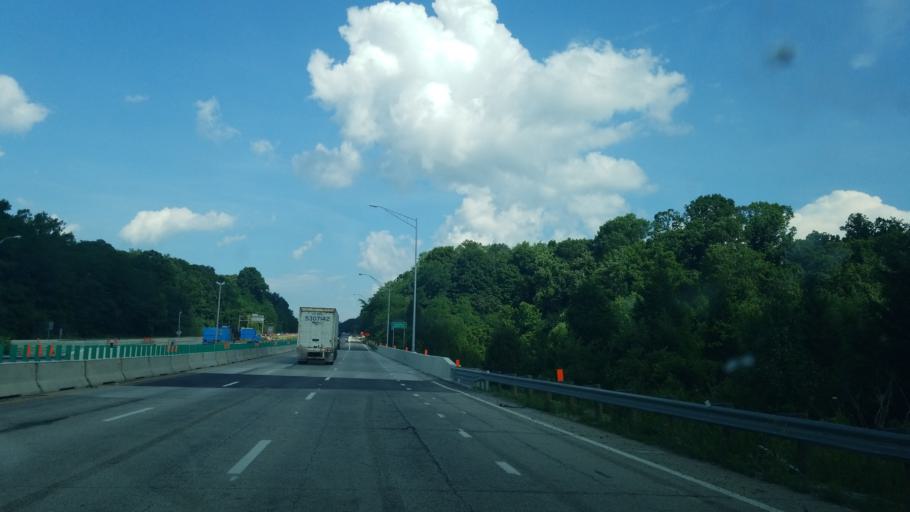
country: US
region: Kentucky
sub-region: Campbell County
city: Silver Grove
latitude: 39.0588
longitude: -84.4145
